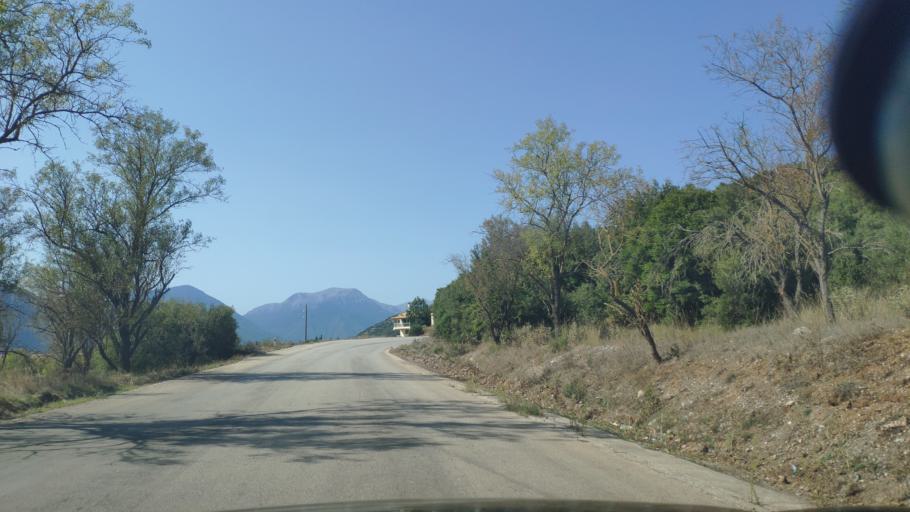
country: GR
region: Peloponnese
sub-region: Nomos Korinthias
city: Nemea
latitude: 37.8908
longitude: 22.5145
